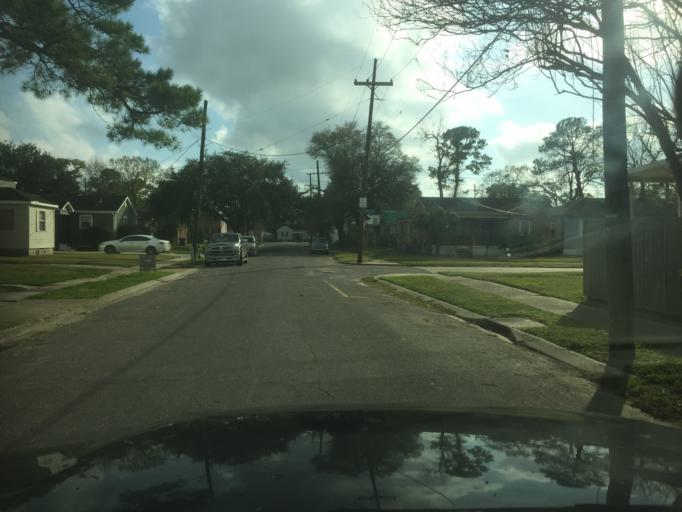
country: US
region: Louisiana
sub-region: Orleans Parish
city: New Orleans
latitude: 29.9901
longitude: -90.0807
